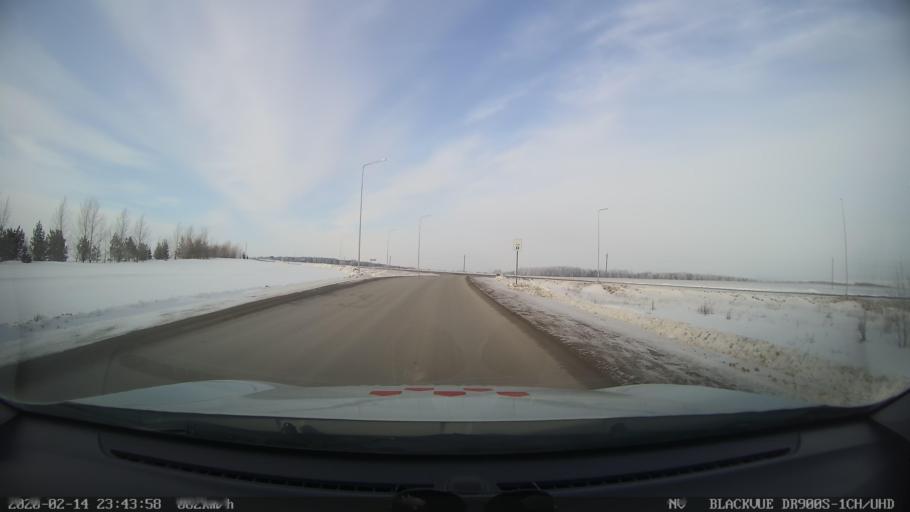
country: RU
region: Tatarstan
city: Kuybyshevskiy Zaton
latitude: 55.2084
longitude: 49.2472
